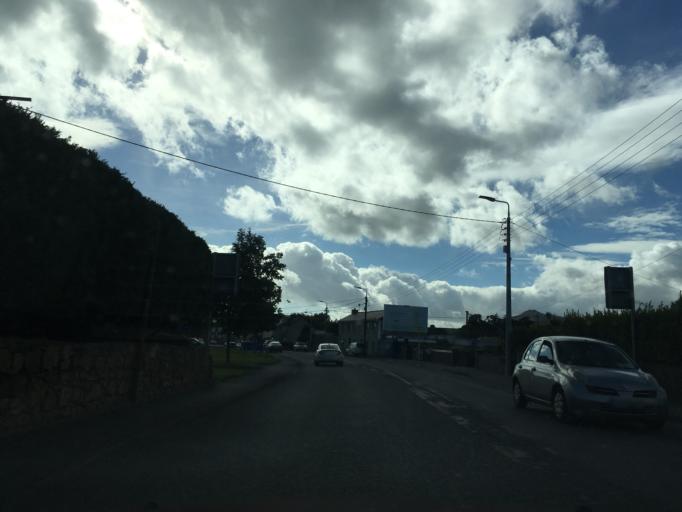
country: IE
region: Leinster
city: Little Bray
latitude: 53.2116
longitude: -6.1179
